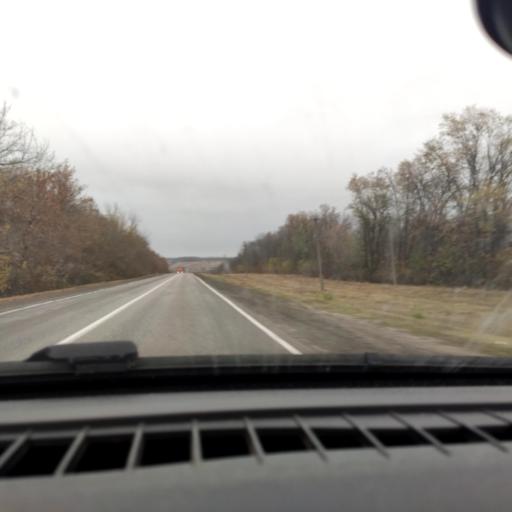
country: RU
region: Voronezj
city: Uryv-Pokrovka
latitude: 51.1117
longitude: 39.0262
